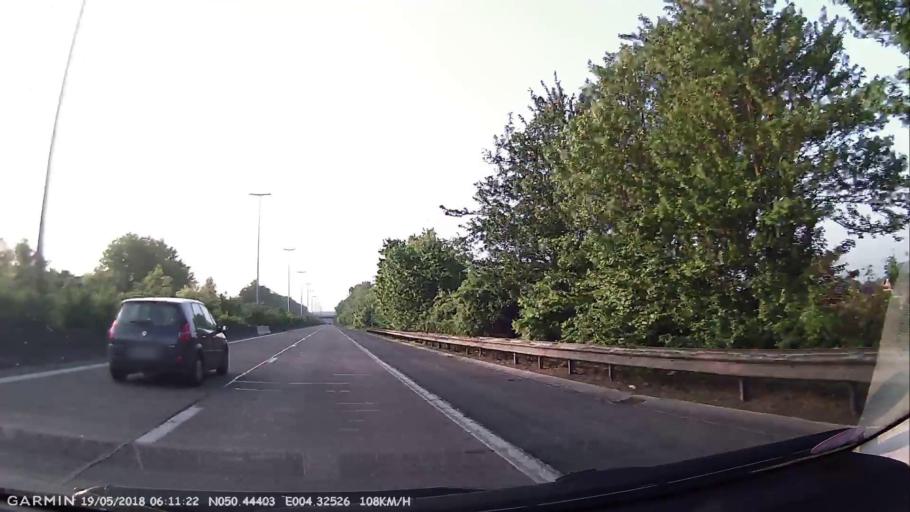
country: BE
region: Wallonia
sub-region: Province du Hainaut
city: Chapelle-lez-Herlaimont
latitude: 50.4440
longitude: 4.3254
